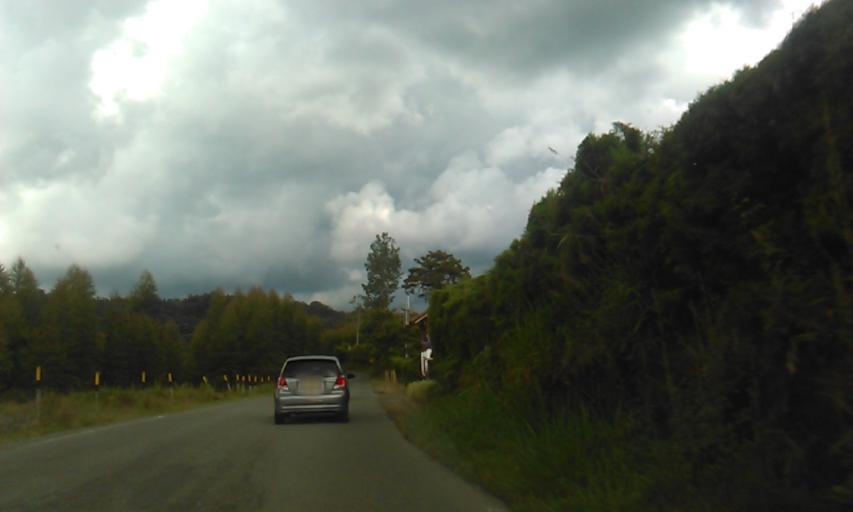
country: CO
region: Quindio
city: Salento
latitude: 4.6422
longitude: -75.5896
